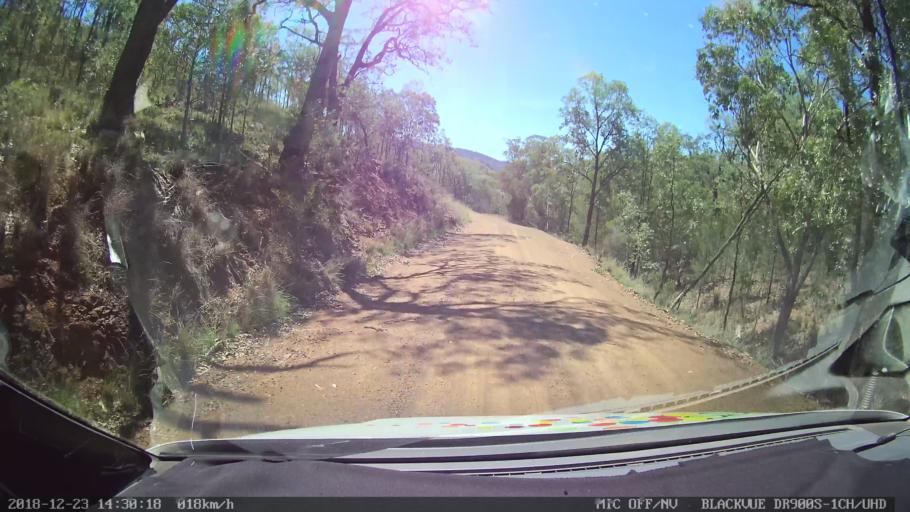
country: AU
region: New South Wales
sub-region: Tamworth Municipality
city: Manilla
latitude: -30.6046
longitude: 150.9332
